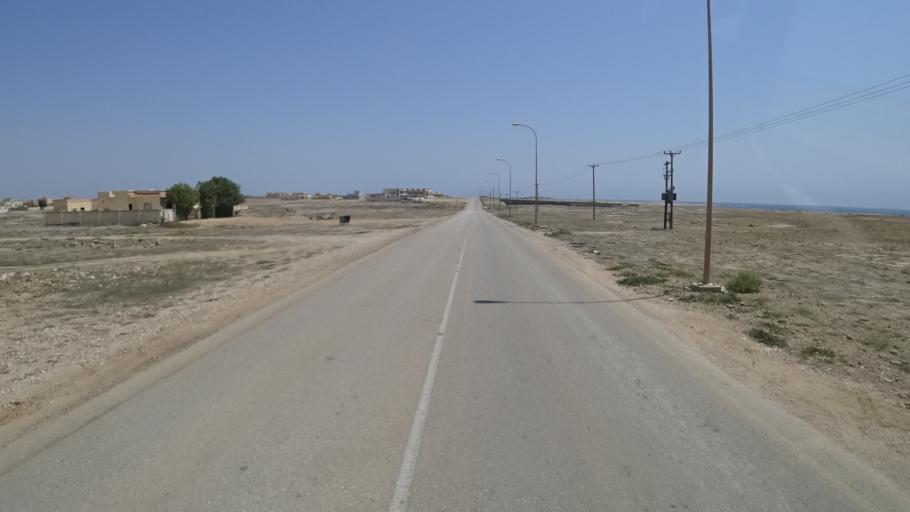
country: OM
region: Zufar
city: Salalah
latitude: 16.9780
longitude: 54.7108
